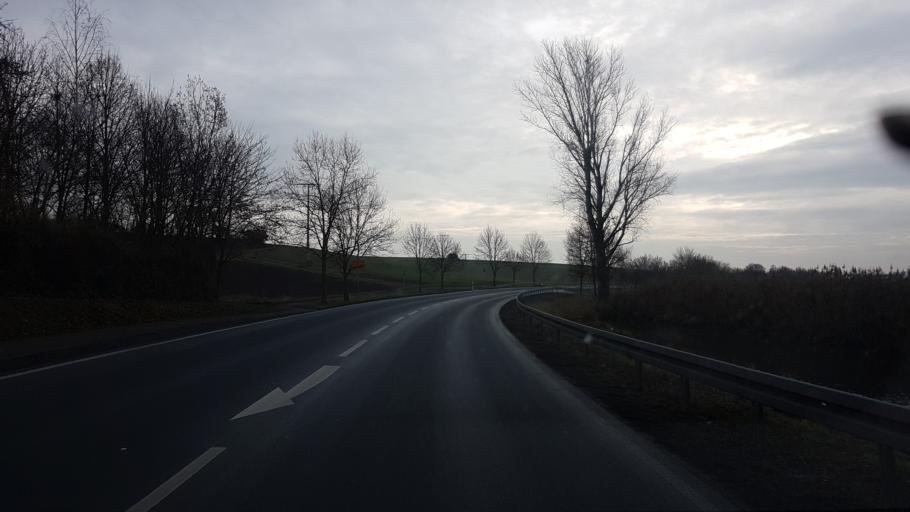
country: DE
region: Bavaria
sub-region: Regierungsbezirk Unterfranken
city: Pfarrweisach
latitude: 50.1581
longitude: 10.7338
